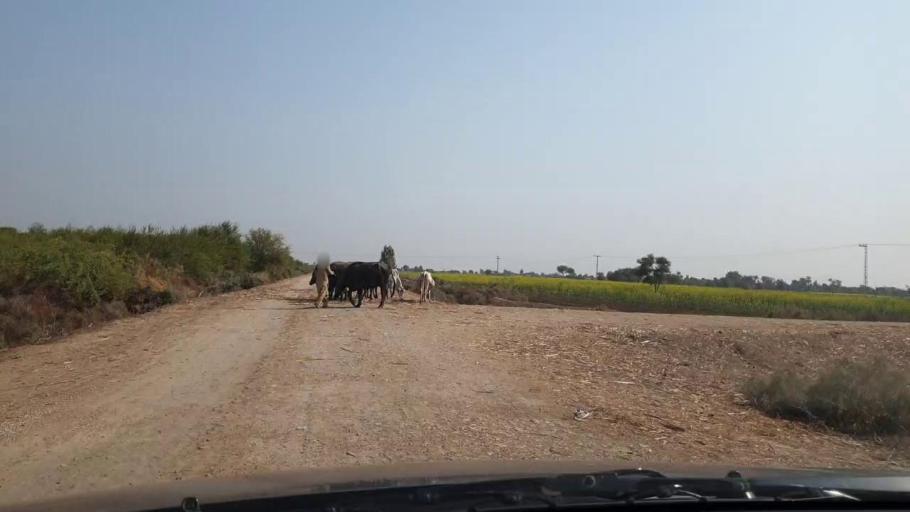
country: PK
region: Sindh
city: Jhol
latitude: 25.9954
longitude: 68.9230
